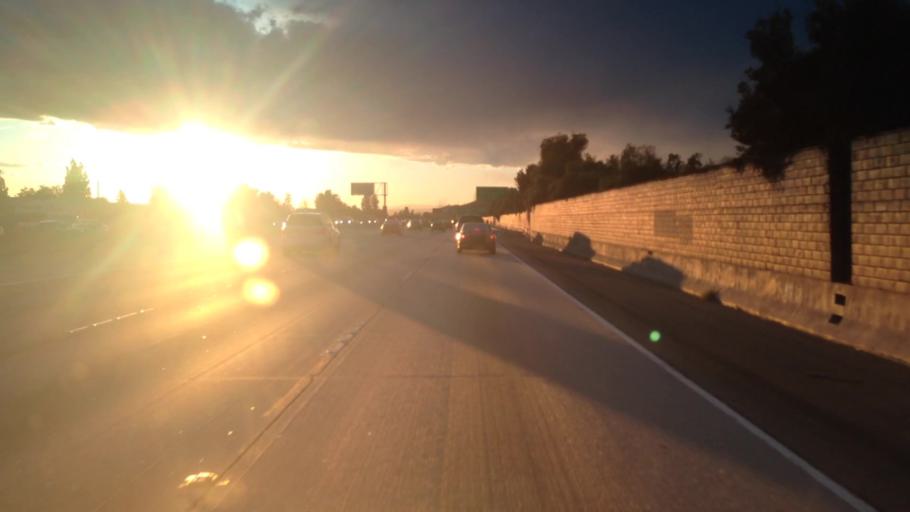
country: US
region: California
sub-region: Los Angeles County
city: San Dimas
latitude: 34.1200
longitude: -117.7972
